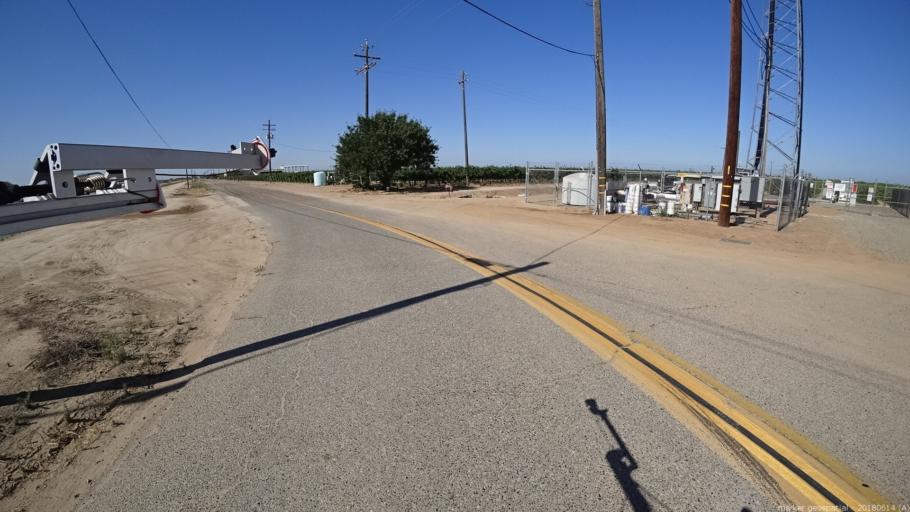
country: US
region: California
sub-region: Madera County
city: Fairmead
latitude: 37.0477
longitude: -120.1659
